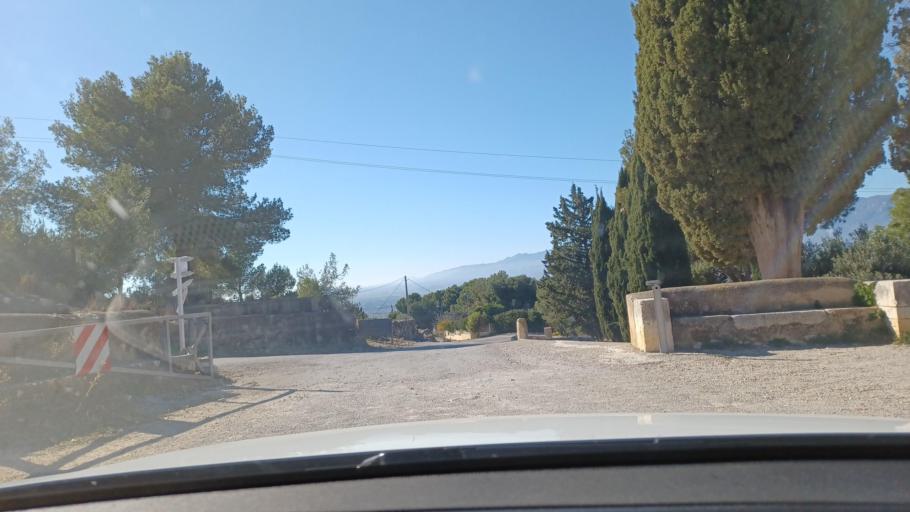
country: ES
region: Catalonia
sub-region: Provincia de Tarragona
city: Tortosa
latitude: 40.8130
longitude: 0.5512
